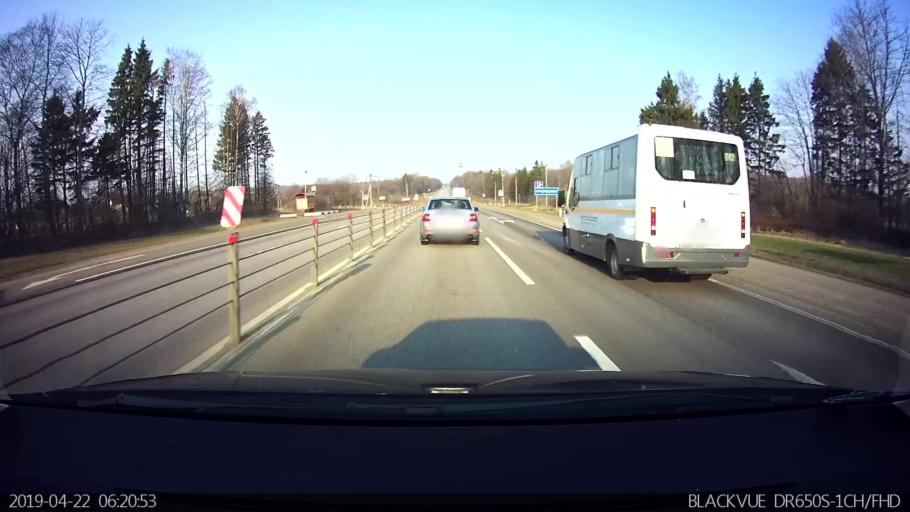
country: RU
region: Moskovskaya
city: Mozhaysk
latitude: 55.4652
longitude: 35.8897
